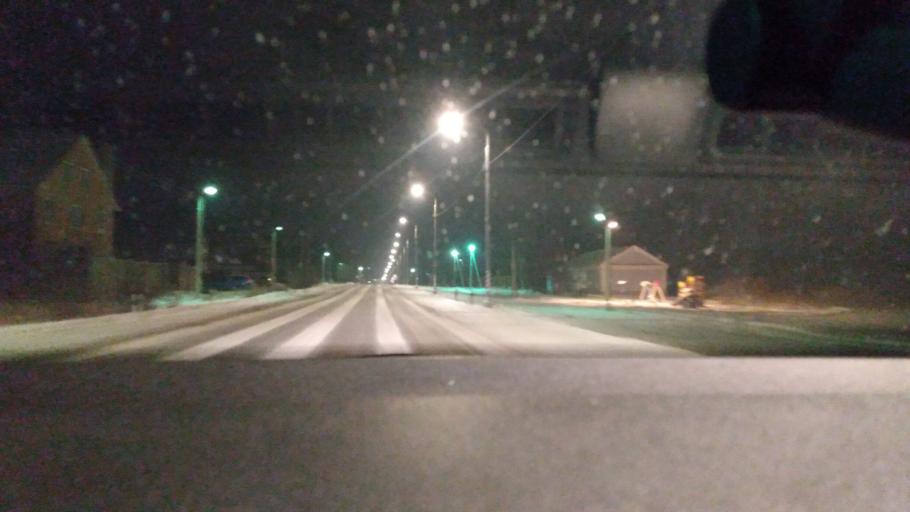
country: RU
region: Moskovskaya
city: Lukhovitsy
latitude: 55.0900
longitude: 38.9421
